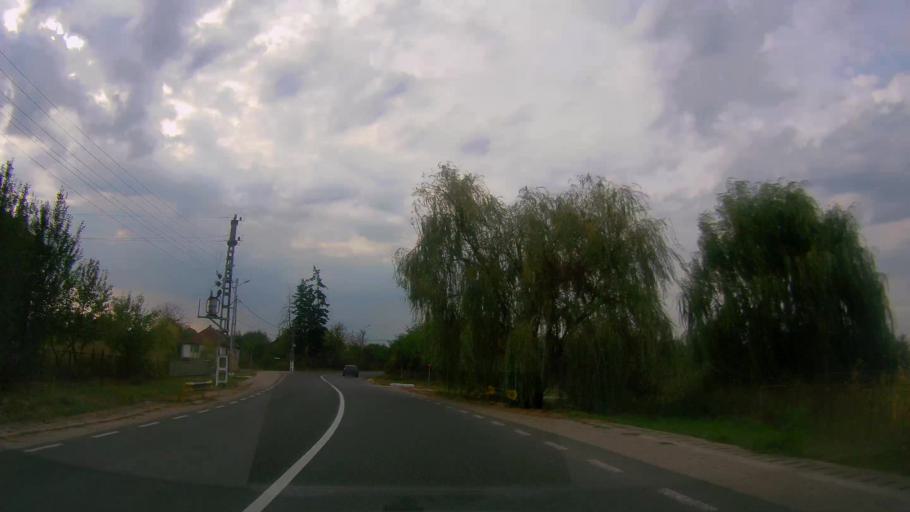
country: RO
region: Satu Mare
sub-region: Comuna Beltiug
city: Beltiug
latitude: 47.5802
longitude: 22.8802
